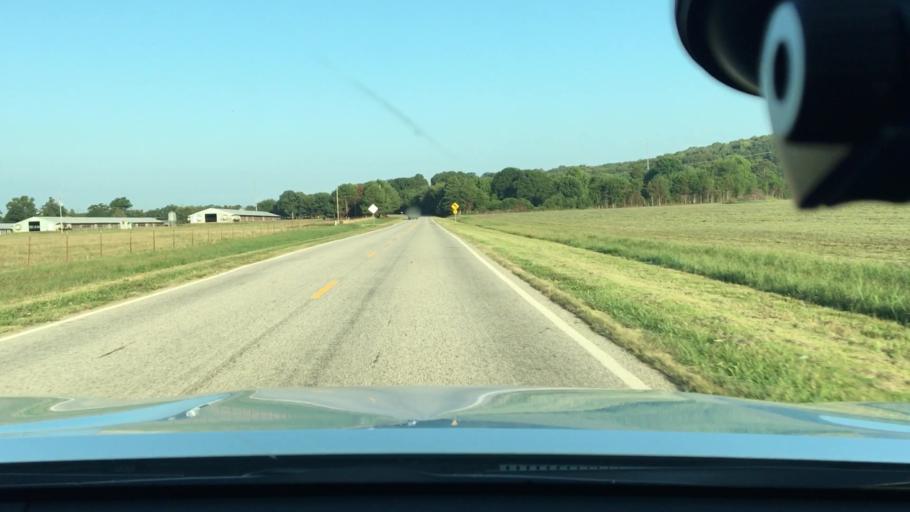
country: US
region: Arkansas
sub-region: Johnson County
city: Coal Hill
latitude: 35.3575
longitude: -93.5557
